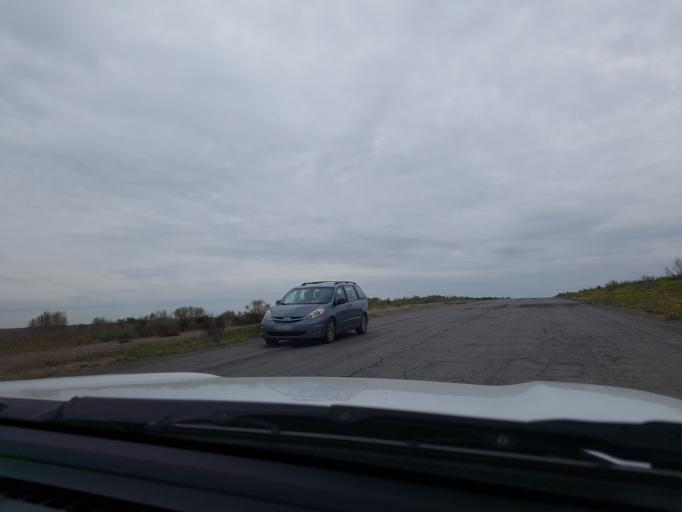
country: TM
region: Mary
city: Bayramaly
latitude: 37.8853
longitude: 62.6144
